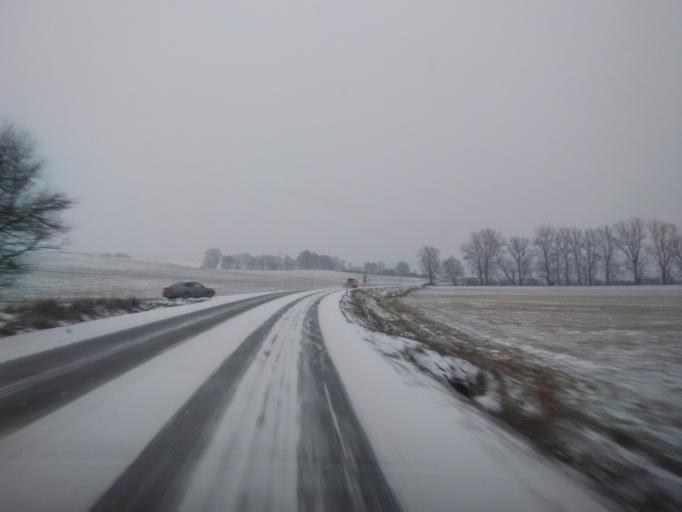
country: CZ
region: Olomoucky
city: Belotin
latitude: 49.5388
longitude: 17.7976
